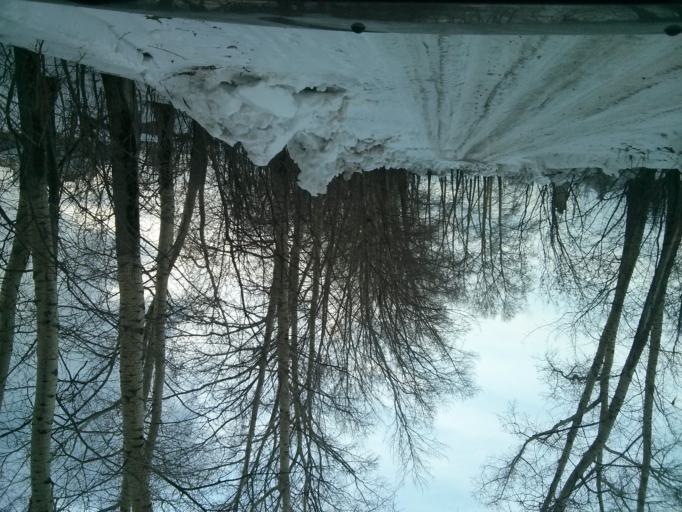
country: RU
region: Nizjnij Novgorod
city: Afonino
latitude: 56.2693
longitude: 44.0317
